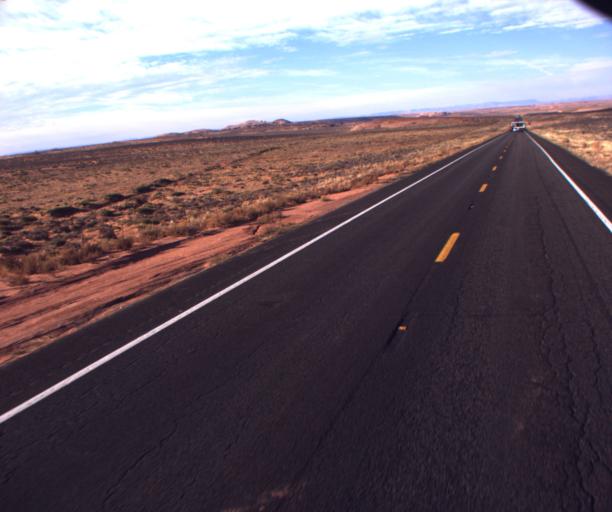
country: US
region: Arizona
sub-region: Apache County
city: Many Farms
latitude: 36.9388
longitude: -109.5511
